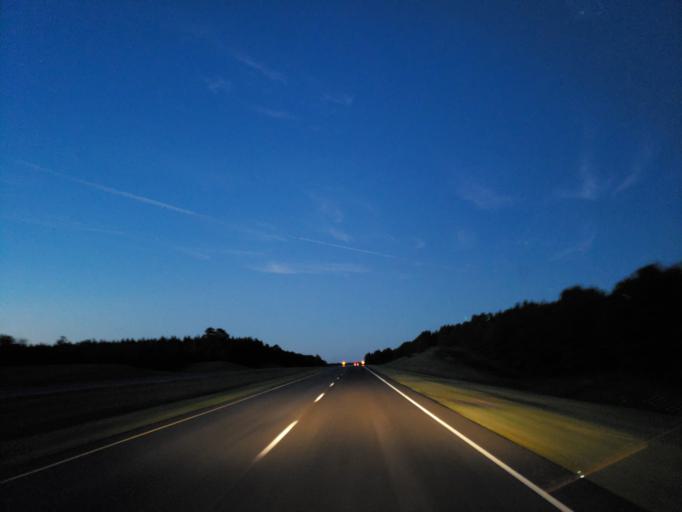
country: US
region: Mississippi
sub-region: Clarke County
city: Quitman
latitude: 32.0196
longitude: -88.6854
